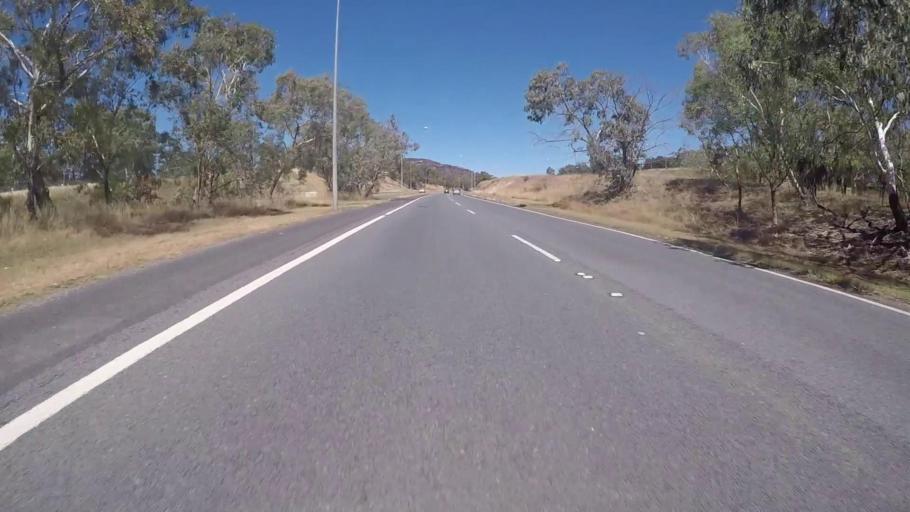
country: AU
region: Australian Capital Territory
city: Forrest
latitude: -35.3505
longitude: 149.0703
